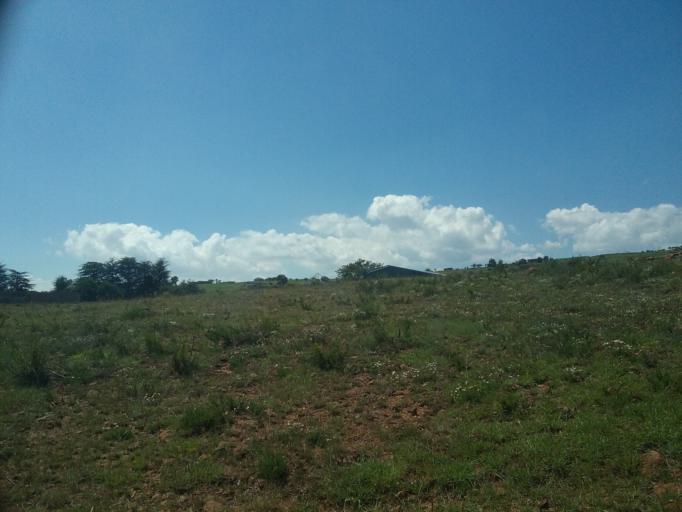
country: LS
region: Berea
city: Teyateyaneng
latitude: -29.2130
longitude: 27.8617
